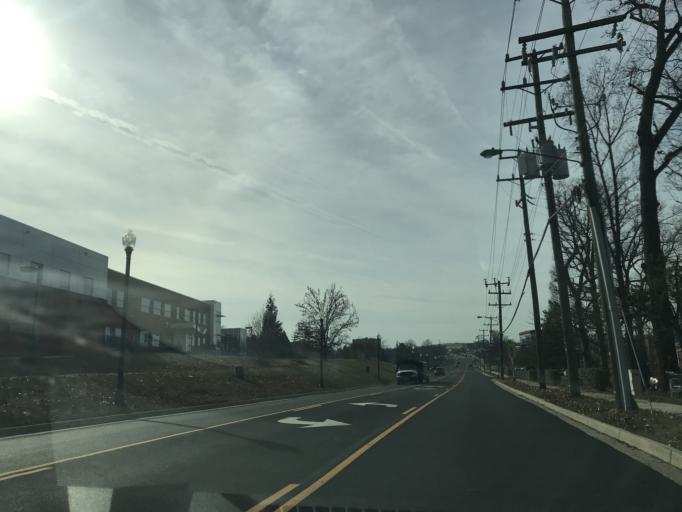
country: US
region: Virginia
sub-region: City of Fairfax
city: Fairfax
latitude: 38.8610
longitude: -77.3277
